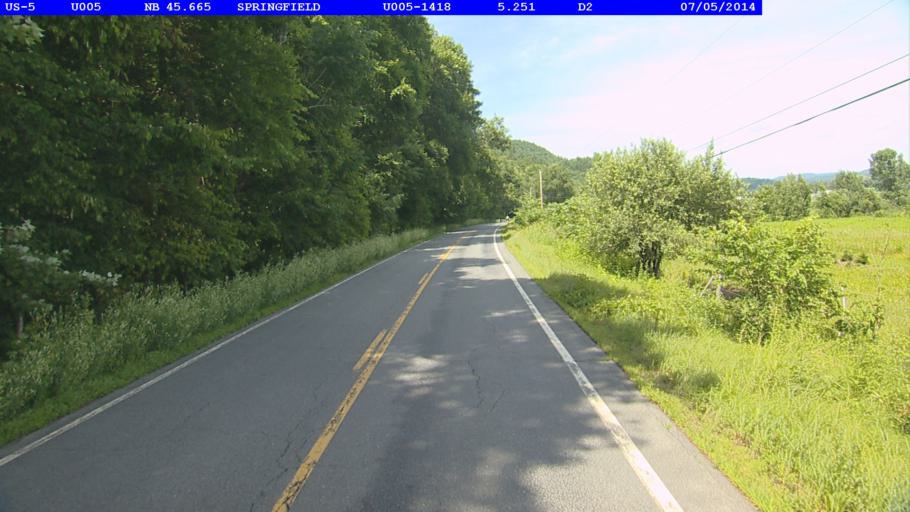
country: US
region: New Hampshire
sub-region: Sullivan County
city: Charlestown
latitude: 43.2894
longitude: -72.4133
